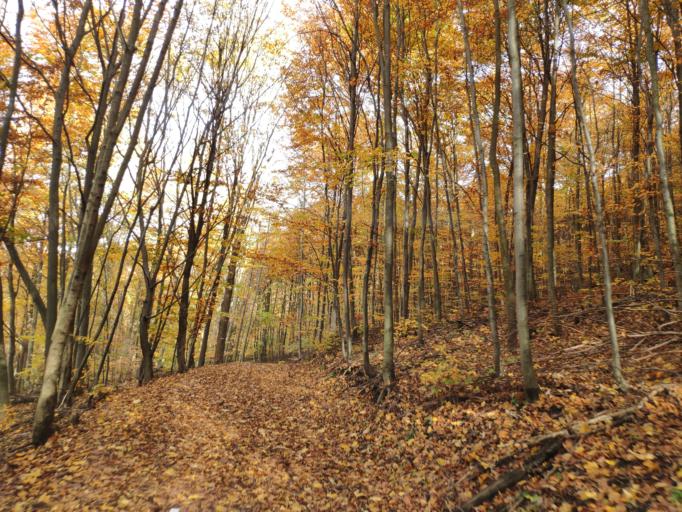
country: SK
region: Presovsky
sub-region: Okres Presov
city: Presov
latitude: 48.8539
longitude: 21.1877
